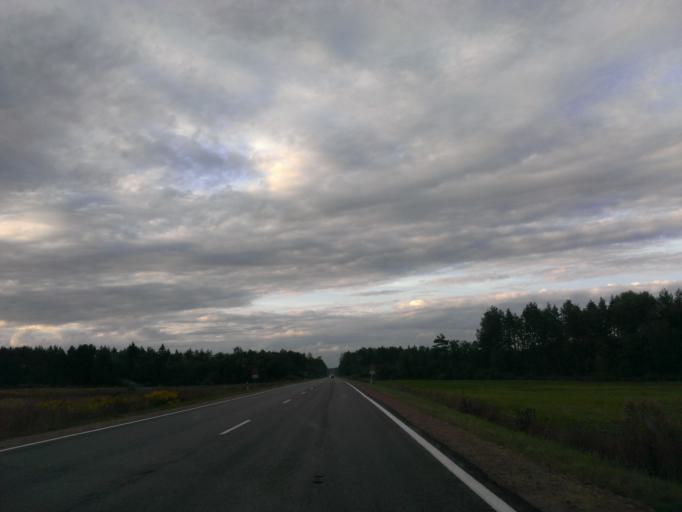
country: LV
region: Salaspils
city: Salaspils
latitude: 56.8830
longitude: 24.4077
